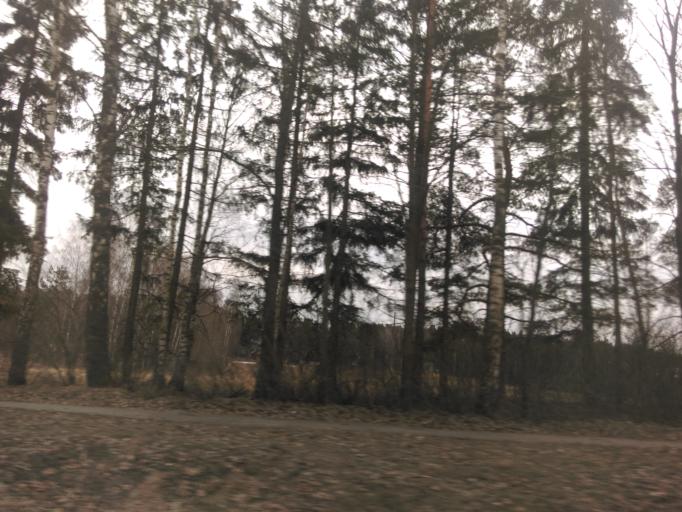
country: RU
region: Moskovskaya
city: Nikolina Gora
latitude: 55.7156
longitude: 37.0865
